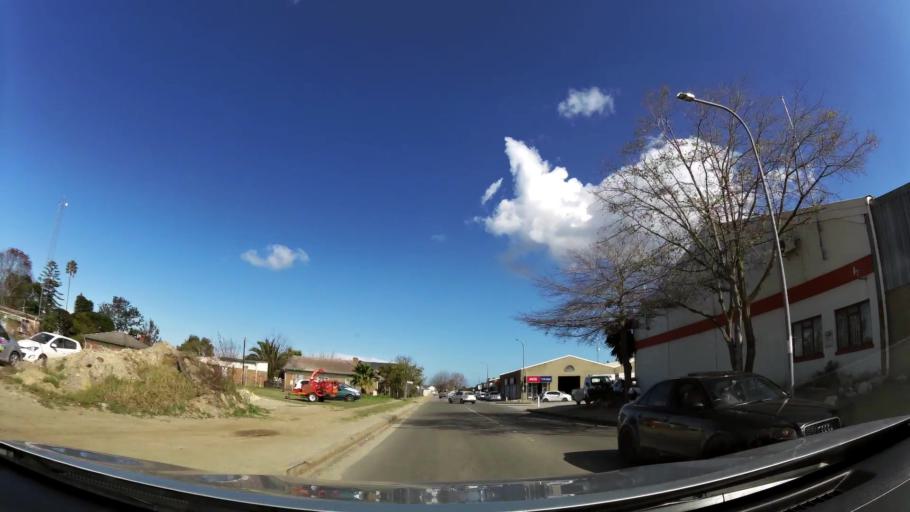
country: ZA
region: Western Cape
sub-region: Eden District Municipality
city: George
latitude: -33.9650
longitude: 22.4672
